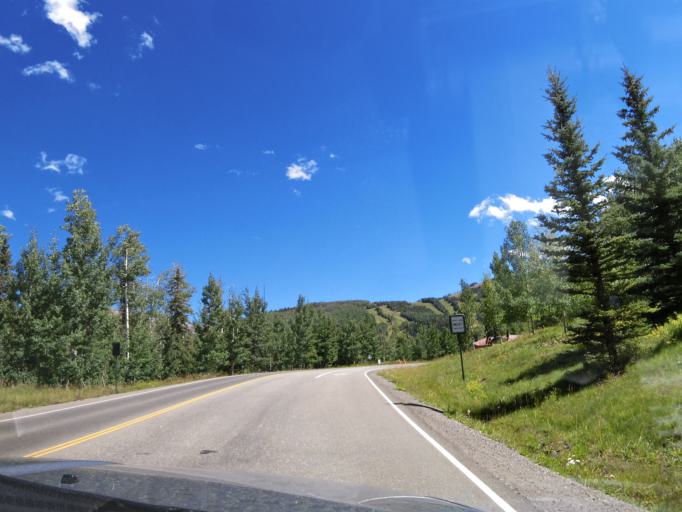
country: US
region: Colorado
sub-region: San Miguel County
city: Mountain Village
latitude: 37.9342
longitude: -107.8580
